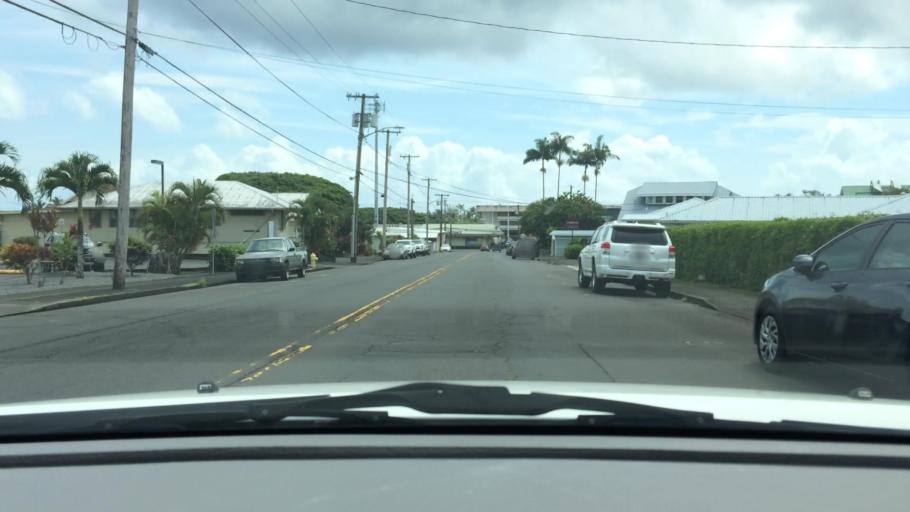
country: US
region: Hawaii
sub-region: Hawaii County
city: Hilo
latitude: 19.7169
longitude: -155.0826
